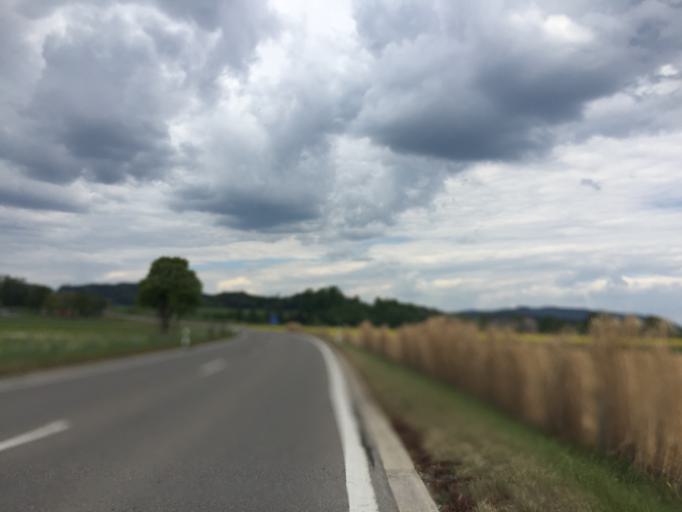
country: CH
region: Bern
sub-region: Thun District
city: Uttigen
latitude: 46.7849
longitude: 7.5803
